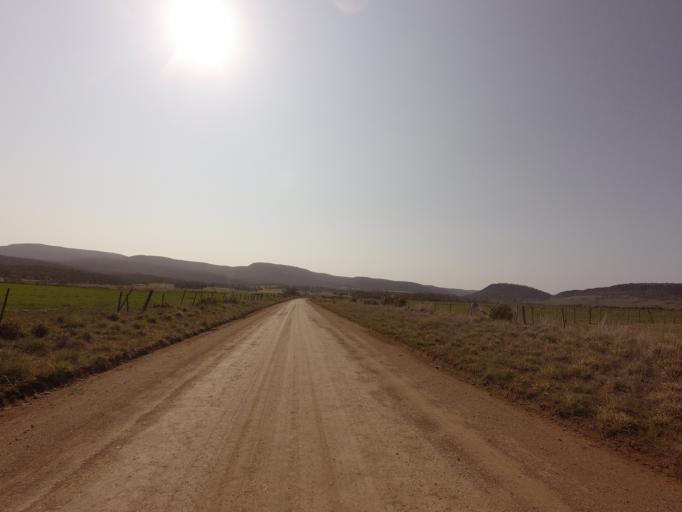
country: AU
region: Tasmania
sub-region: Break O'Day
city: St Helens
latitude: -41.8199
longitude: 147.9354
